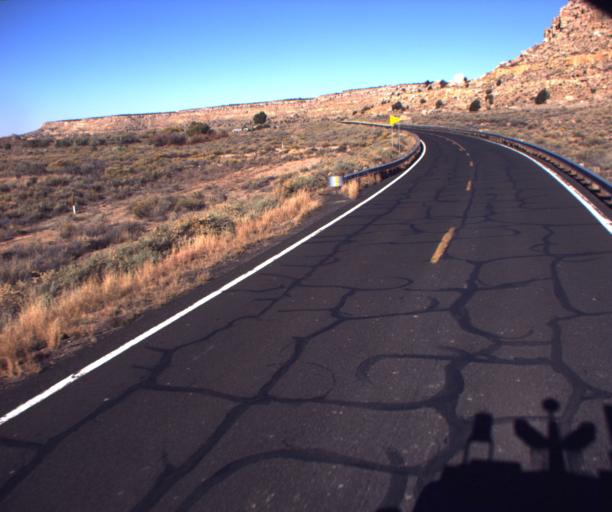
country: US
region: Arizona
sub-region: Navajo County
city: First Mesa
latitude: 35.8385
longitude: -110.2319
